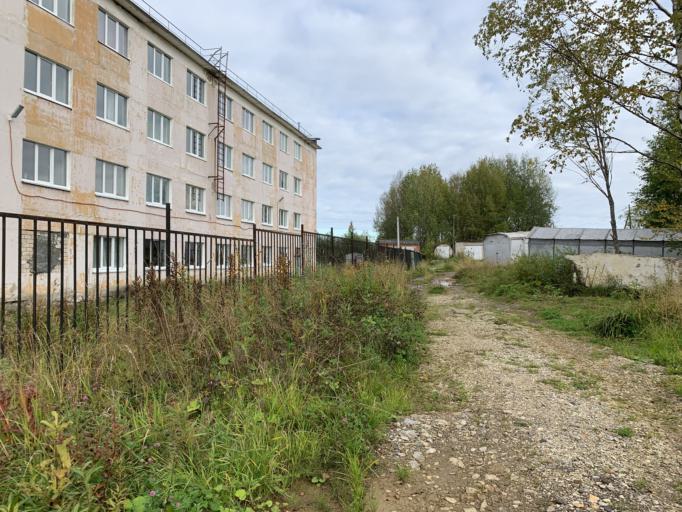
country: RU
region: Perm
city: Gubakha
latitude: 58.8312
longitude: 57.5603
